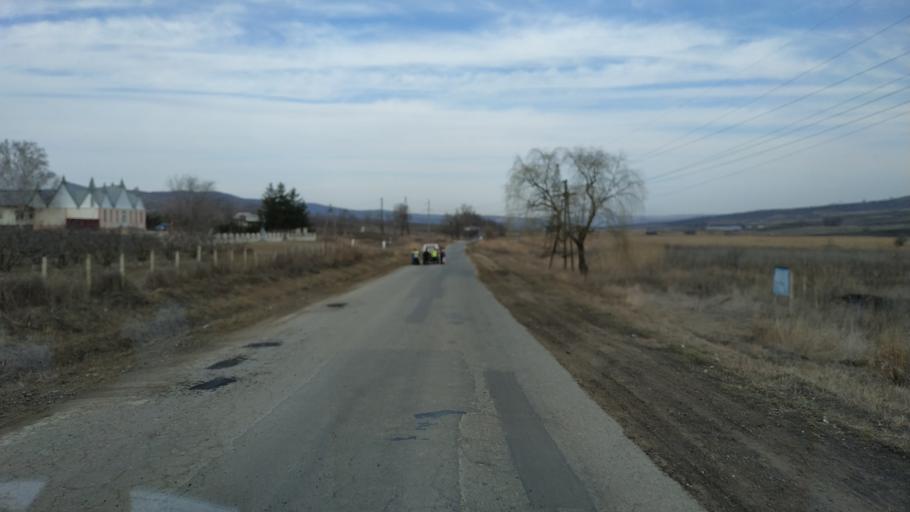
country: MD
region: Nisporeni
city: Nisporeni
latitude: 47.0857
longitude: 28.1405
